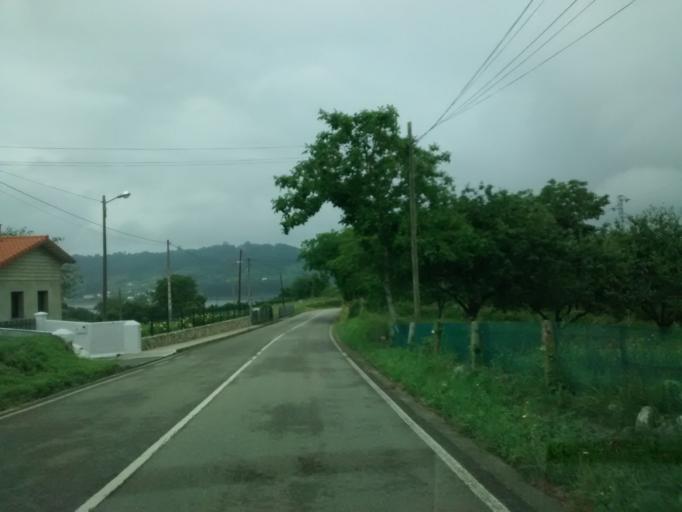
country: ES
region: Asturias
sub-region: Province of Asturias
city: Villaviciosa
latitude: 43.5216
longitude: -5.3696
